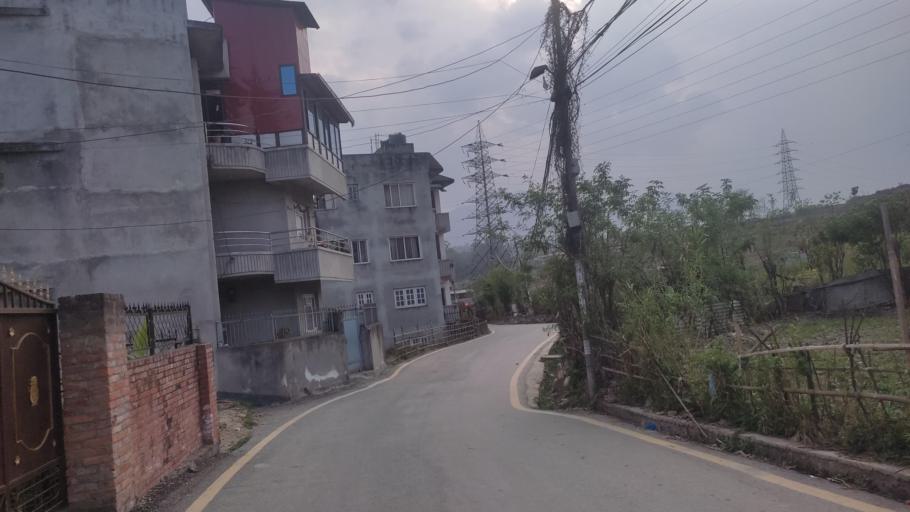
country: NP
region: Central Region
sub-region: Bagmati Zone
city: Patan
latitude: 27.6827
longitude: 85.2955
